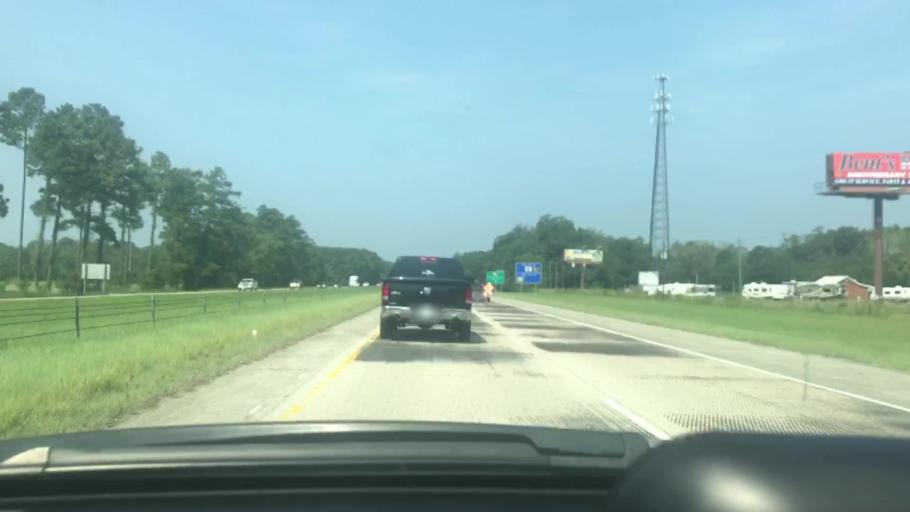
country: US
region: Louisiana
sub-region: Livingston Parish
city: Albany
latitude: 30.4794
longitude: -90.5333
